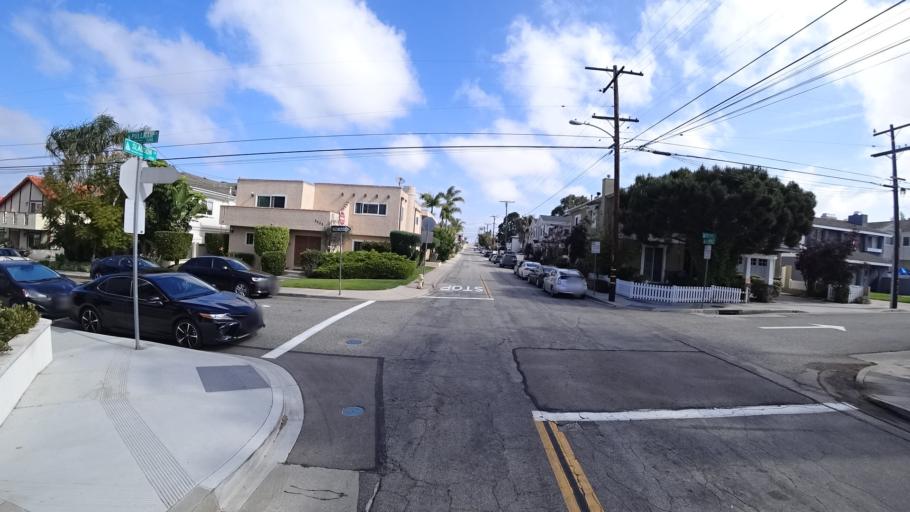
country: US
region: California
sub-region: Los Angeles County
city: Redondo Beach
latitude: 33.8642
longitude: -118.3707
